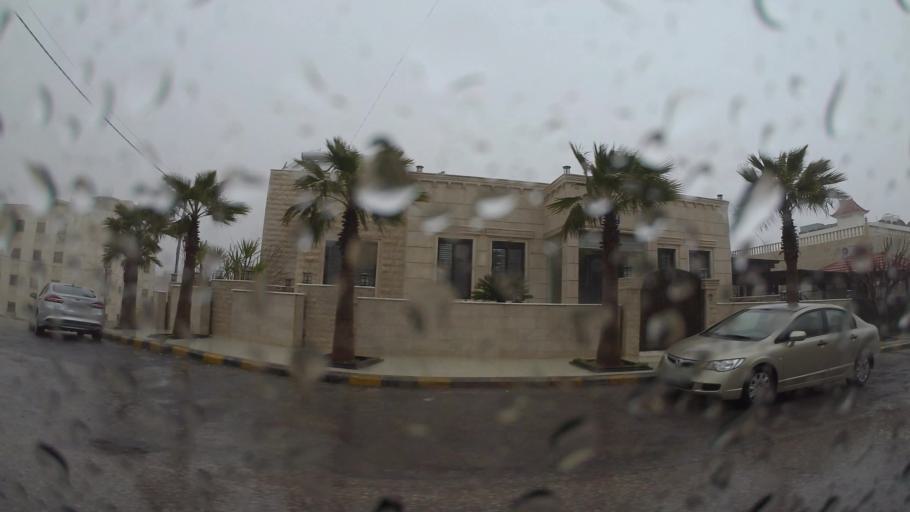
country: JO
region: Amman
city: Al Jubayhah
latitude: 32.0186
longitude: 35.8867
